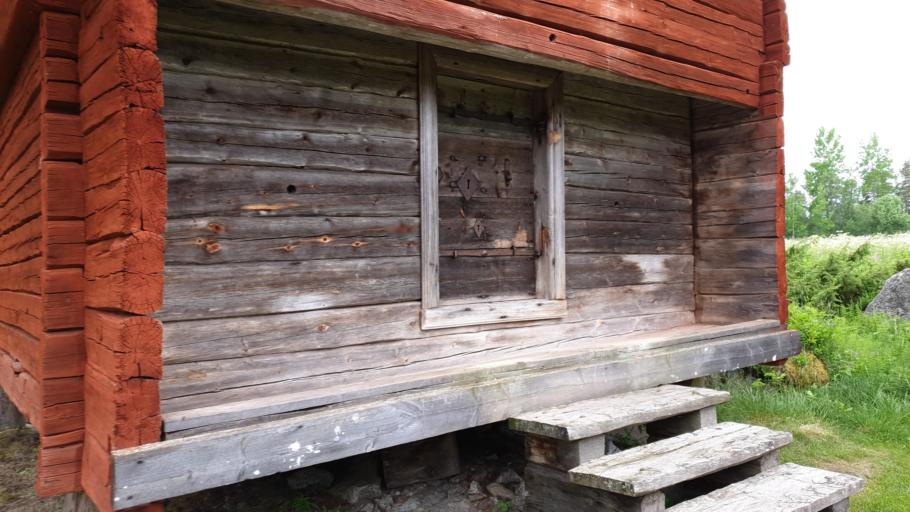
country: SE
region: Jaemtland
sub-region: Harjedalens Kommun
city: Sveg
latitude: 61.7968
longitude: 14.6336
